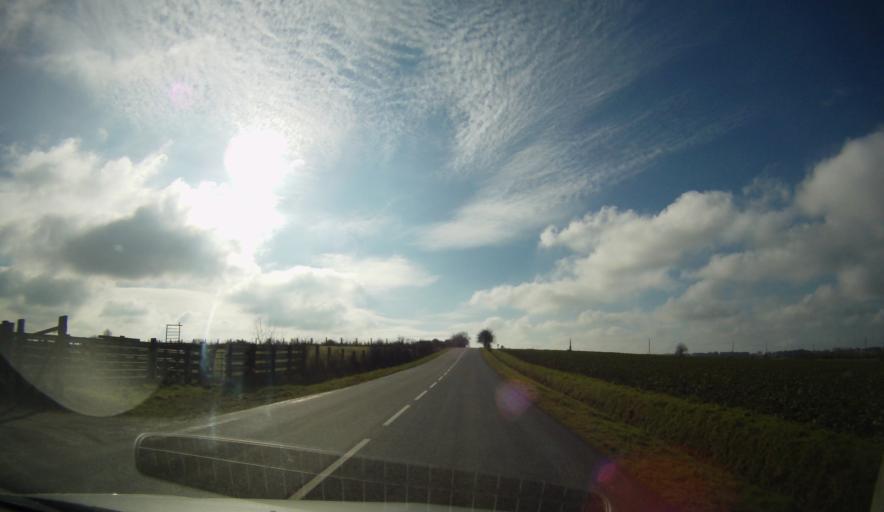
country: FR
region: Brittany
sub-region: Departement d'Ille-et-Vilaine
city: Corps-Nuds
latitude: 47.9382
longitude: -1.5593
